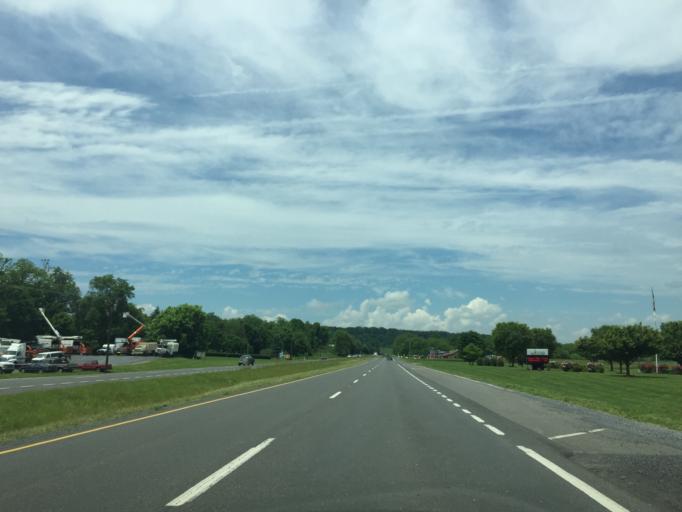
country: US
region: Virginia
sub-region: City of Winchester
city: Winchester
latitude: 39.2189
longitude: -78.1939
